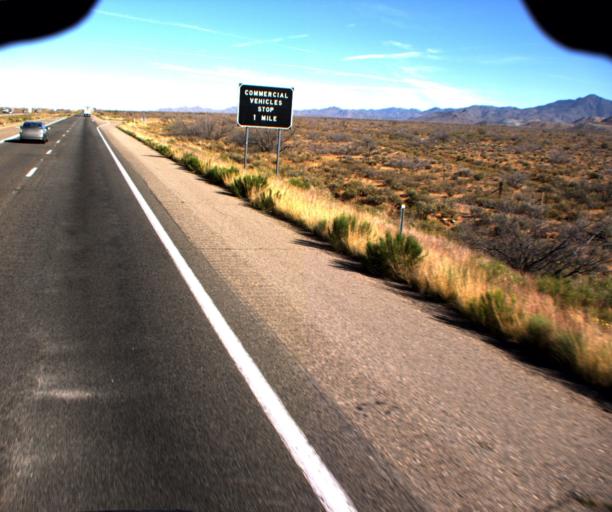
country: US
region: Arizona
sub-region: Mohave County
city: Golden Valley
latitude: 35.2796
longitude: -114.1742
